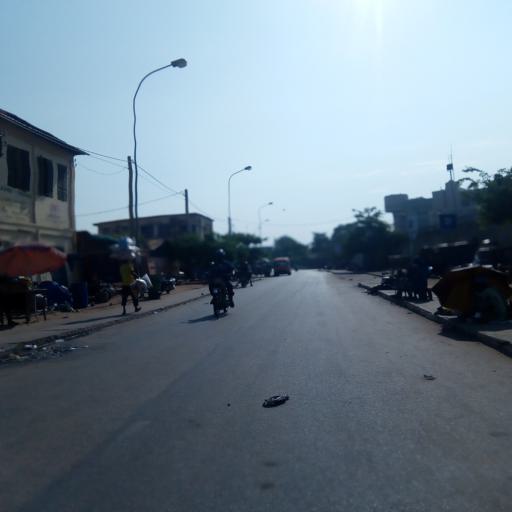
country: TG
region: Maritime
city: Lome
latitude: 6.1347
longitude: 1.2255
